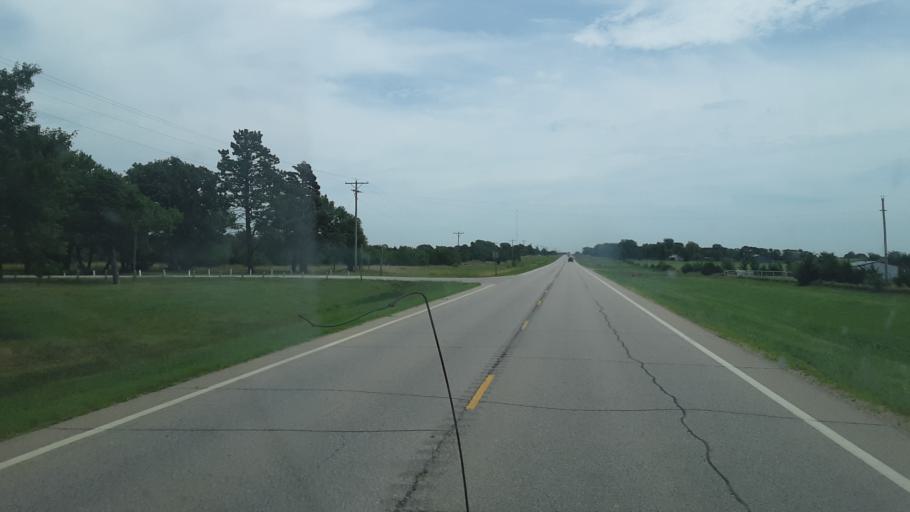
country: US
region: Kansas
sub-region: Butler County
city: El Dorado
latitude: 37.8106
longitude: -96.6603
